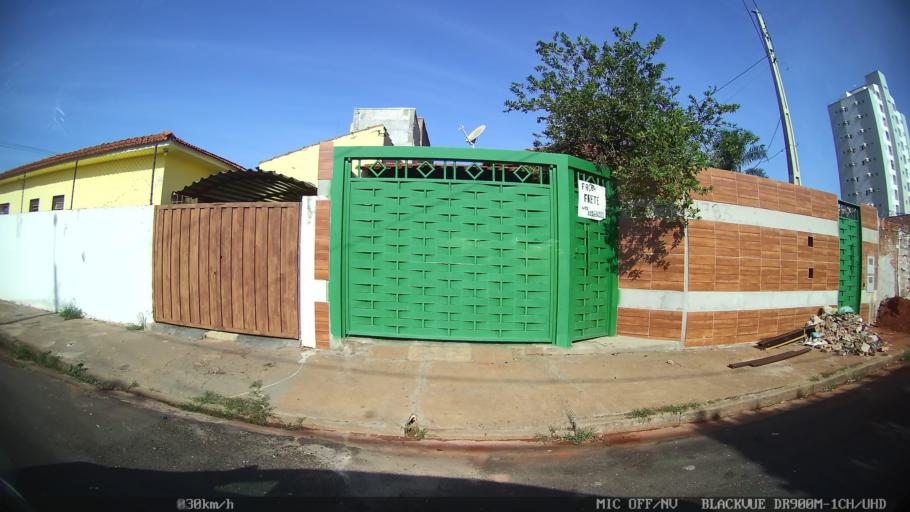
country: BR
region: Sao Paulo
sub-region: Sao Jose Do Rio Preto
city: Sao Jose do Rio Preto
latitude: -20.8008
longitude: -49.3940
